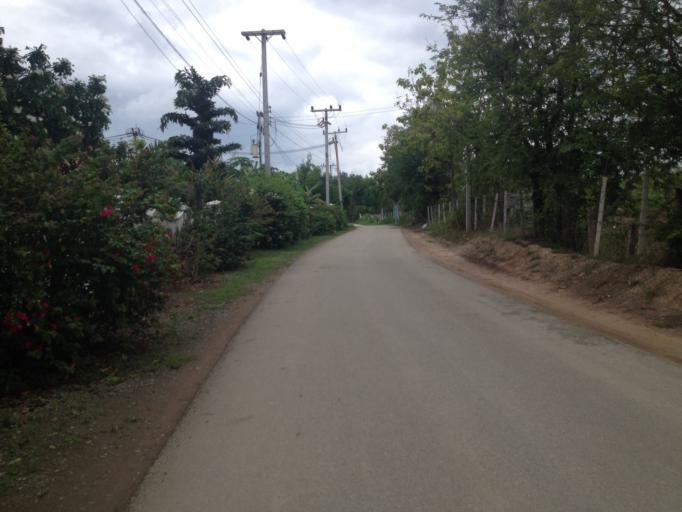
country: TH
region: Chiang Mai
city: Hang Dong
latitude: 18.6952
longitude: 98.8913
